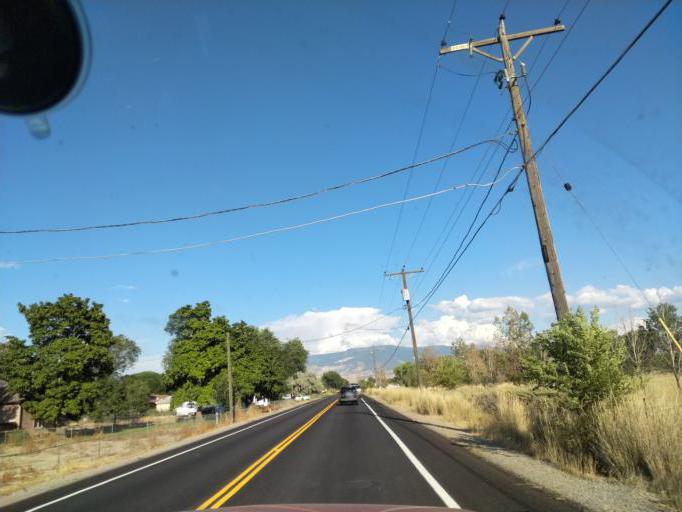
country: US
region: Colorado
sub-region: Mesa County
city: Fruitvale
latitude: 39.0628
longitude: -108.4841
